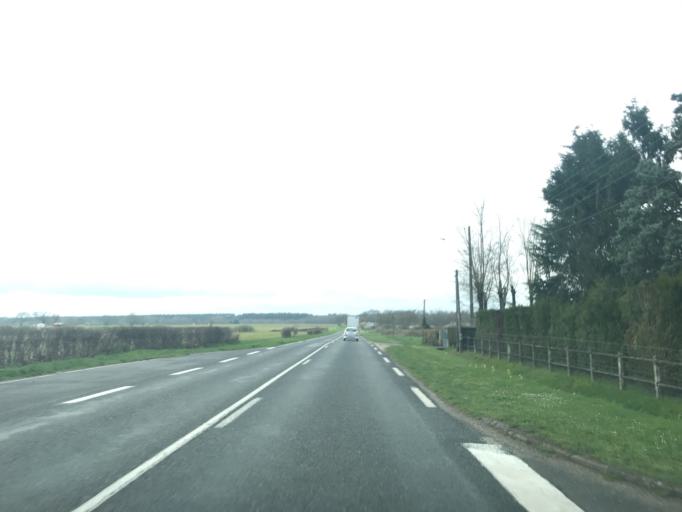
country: FR
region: Centre
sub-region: Departement du Loiret
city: Nevoy
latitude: 47.7183
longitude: 2.5845
